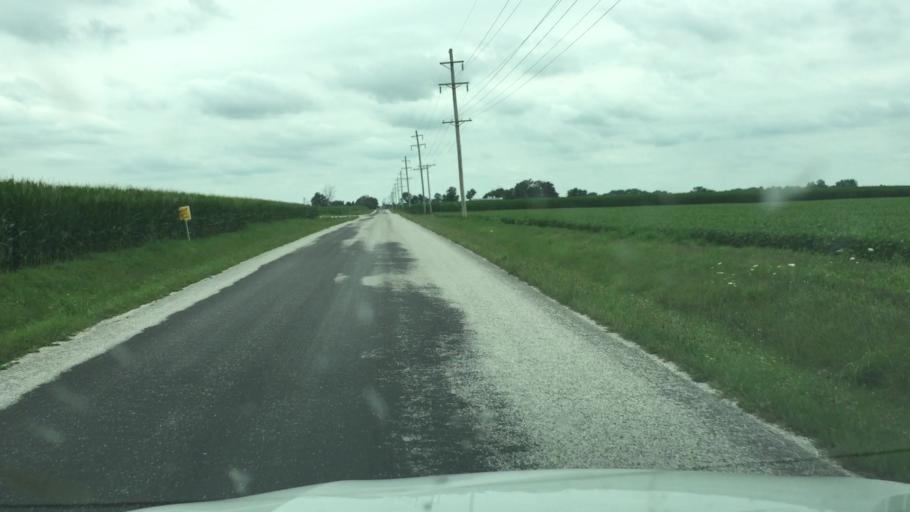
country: US
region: Illinois
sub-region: Hancock County
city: Carthage
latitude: 40.3949
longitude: -91.0826
